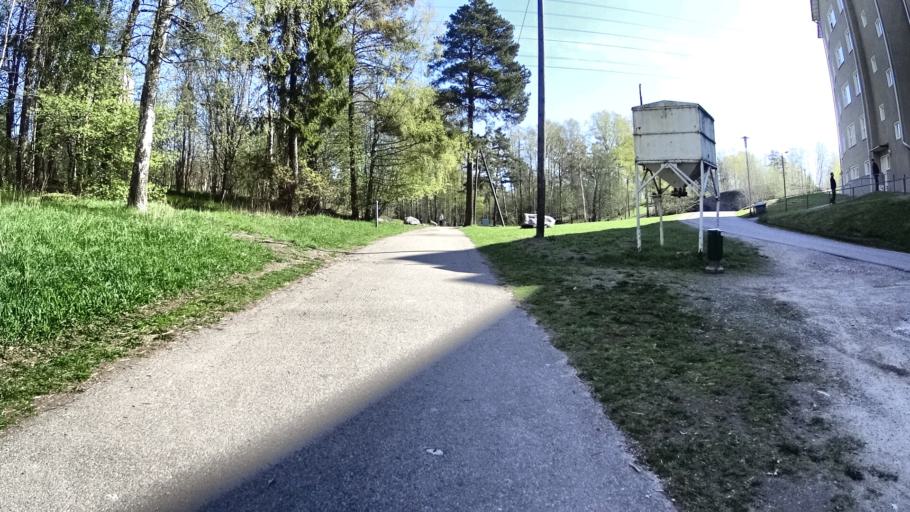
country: FI
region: Uusimaa
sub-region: Helsinki
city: Vantaa
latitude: 60.2103
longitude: 25.0403
